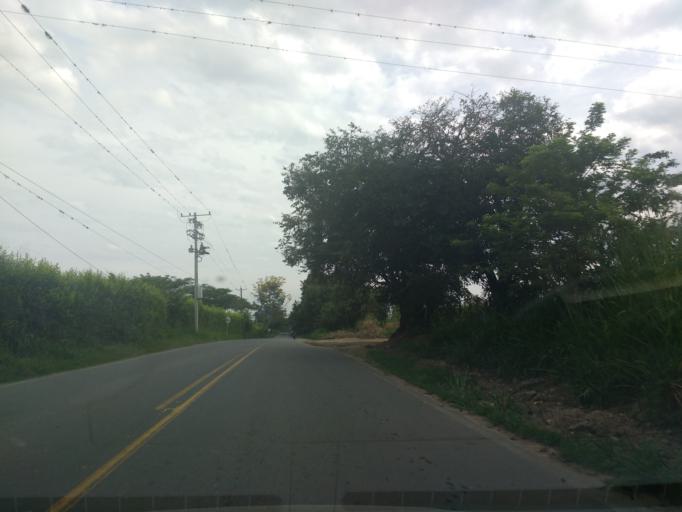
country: CO
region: Valle del Cauca
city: Florida
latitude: 3.2983
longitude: -76.2304
